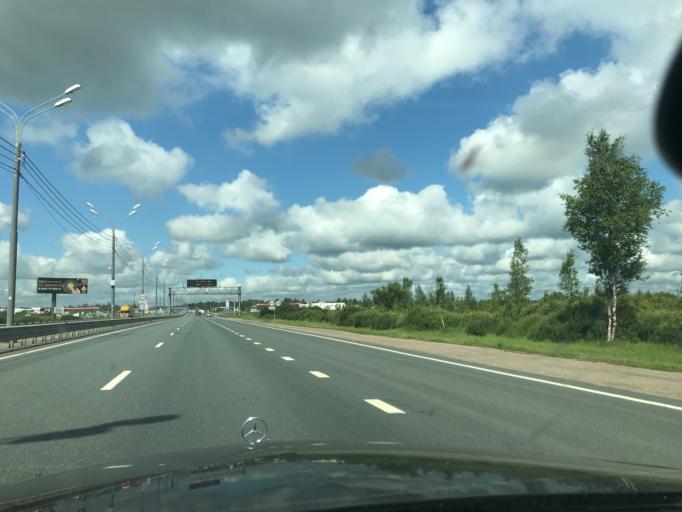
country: RU
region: Smolensk
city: Rudnya
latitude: 54.6908
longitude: 31.0285
